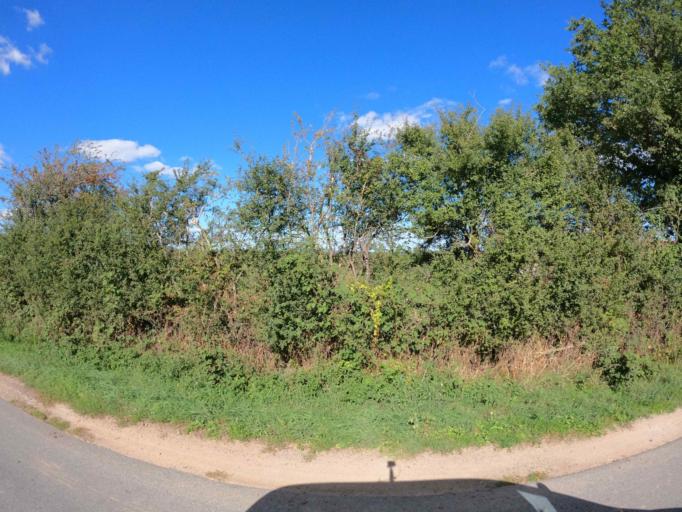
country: FR
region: Auvergne
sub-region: Departement de l'Allier
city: Doyet
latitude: 46.4006
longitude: 2.7463
